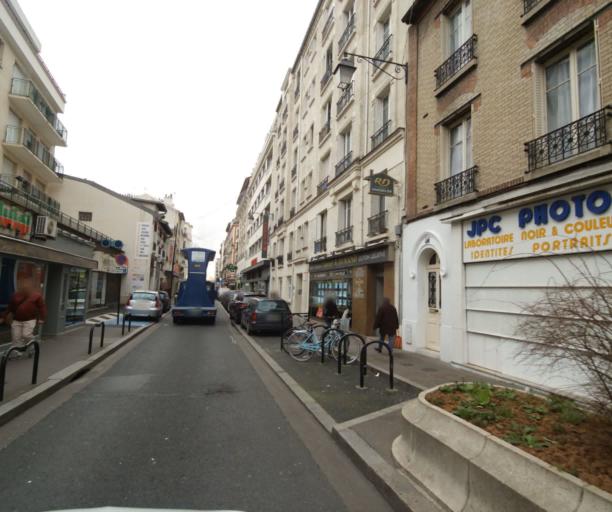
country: FR
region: Ile-de-France
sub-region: Departement des Hauts-de-Seine
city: Courbevoie
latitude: 48.9031
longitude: 2.2682
